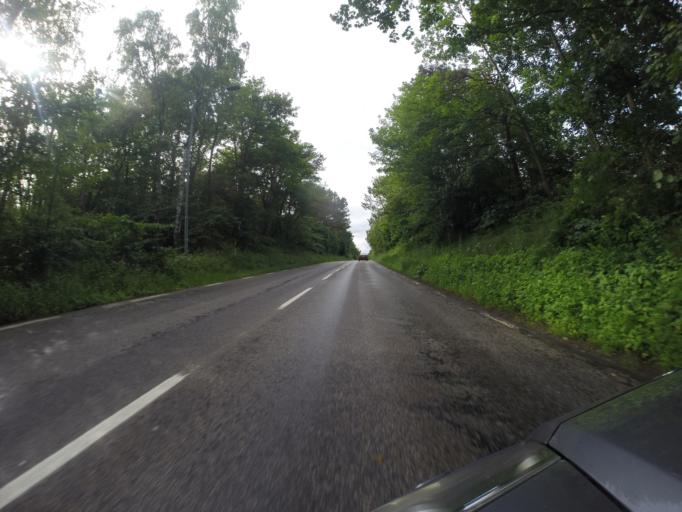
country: SE
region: Skane
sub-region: Kavlinge Kommun
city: Hofterup
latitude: 55.7970
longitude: 12.9912
